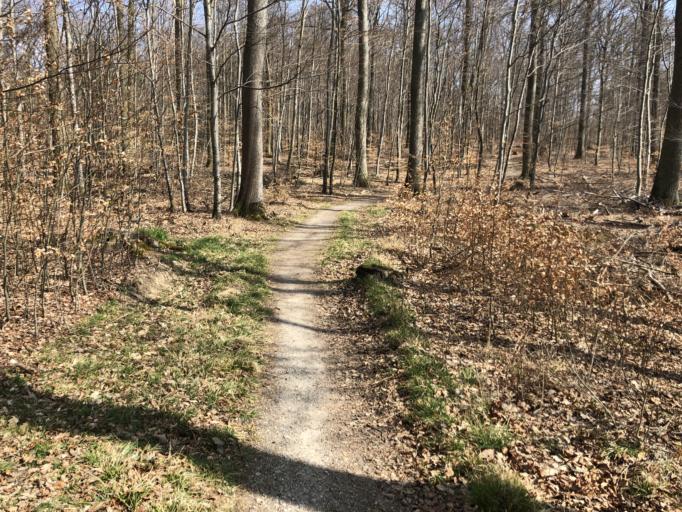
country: DE
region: Baden-Wuerttemberg
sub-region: Tuebingen Region
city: Tuebingen
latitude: 48.5484
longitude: 9.0214
